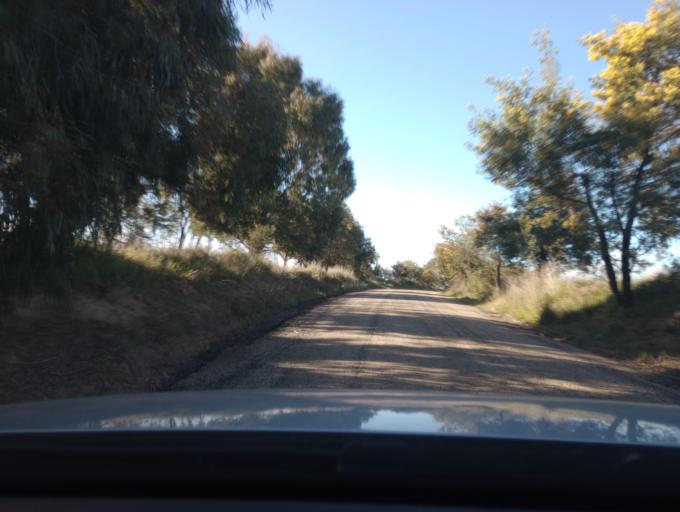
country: AU
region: New South Wales
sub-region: Blayney
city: Millthorpe
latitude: -33.3943
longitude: 149.3097
